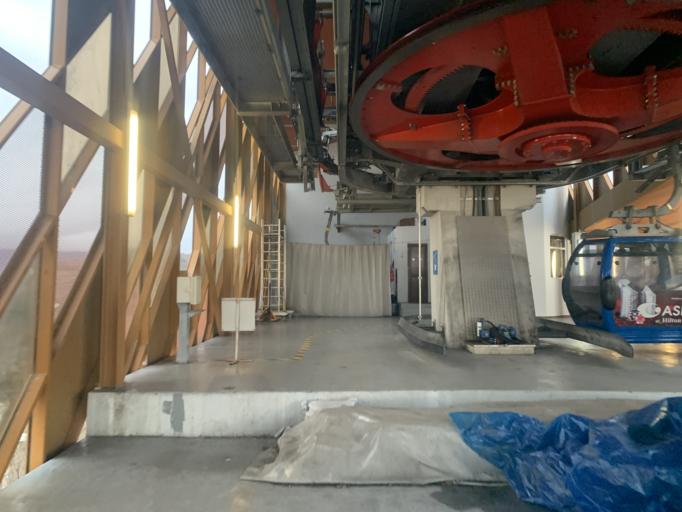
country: GE
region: Ajaria
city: Batumi
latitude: 41.6258
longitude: 41.6564
